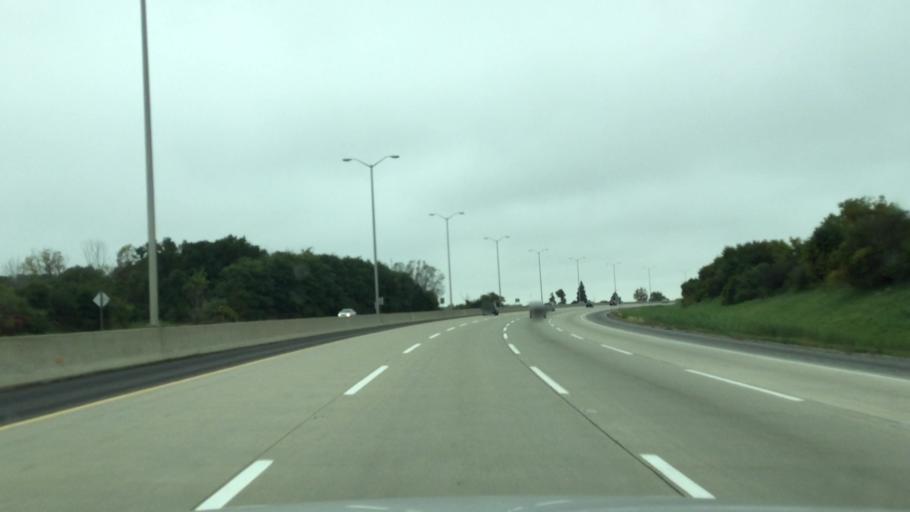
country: US
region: Illinois
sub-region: Lake County
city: Wadsworth
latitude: 42.4701
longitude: -87.9634
